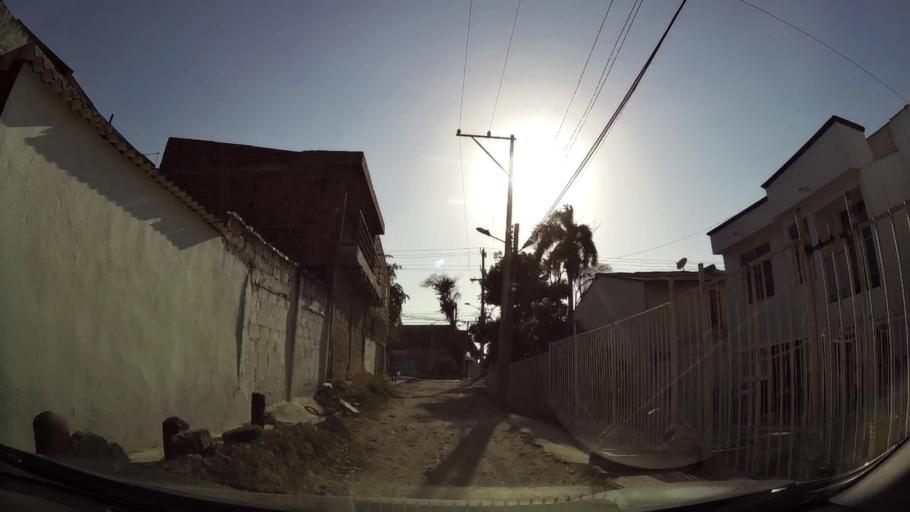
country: CO
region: Bolivar
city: Cartagena
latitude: 10.4007
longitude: -75.4809
